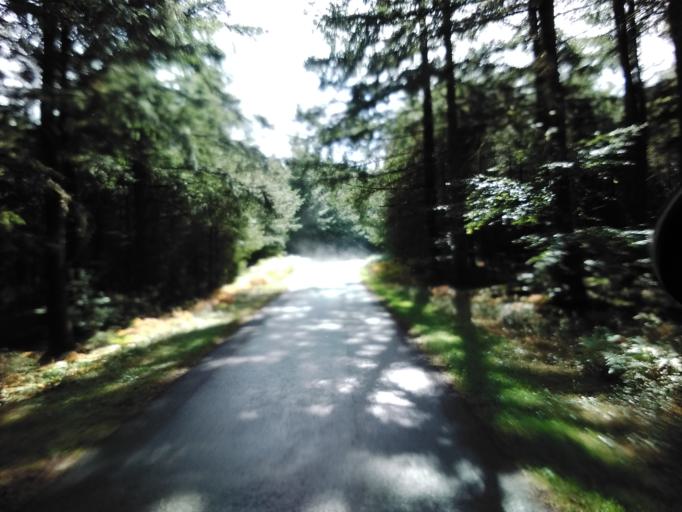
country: FR
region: Bourgogne
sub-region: Departement de la Nievre
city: Lormes
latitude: 47.3167
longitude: 3.8966
